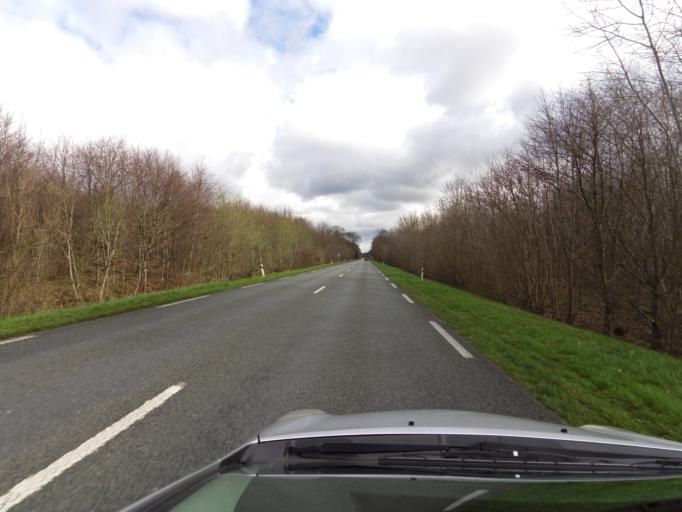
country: FR
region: Picardie
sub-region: Departement de l'Oise
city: Fleurines
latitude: 49.2792
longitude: 2.5963
